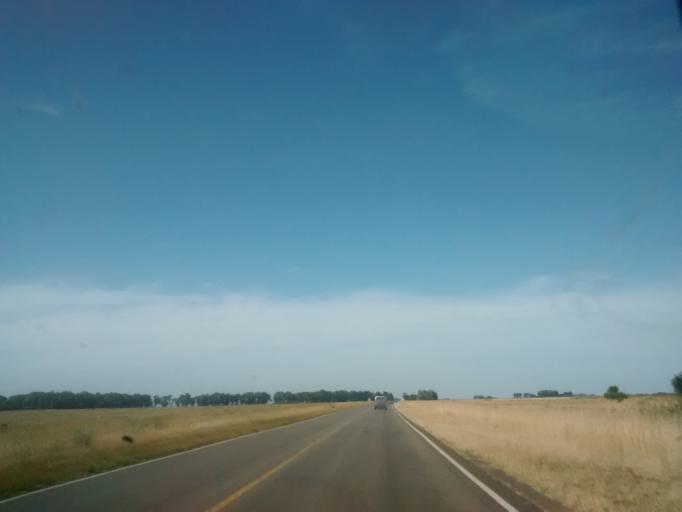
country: AR
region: Buenos Aires
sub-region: Partido de Ayacucho
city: Ayacucho
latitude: -37.3753
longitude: -58.4807
